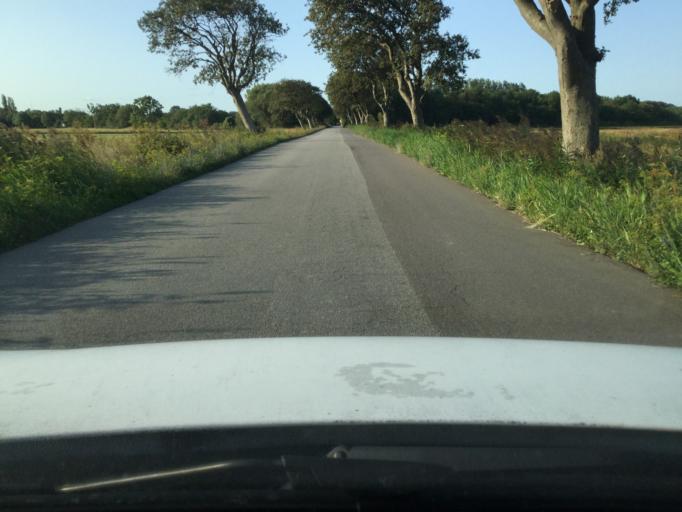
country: DK
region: Zealand
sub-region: Lolland Kommune
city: Rodby
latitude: 54.7021
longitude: 11.3883
